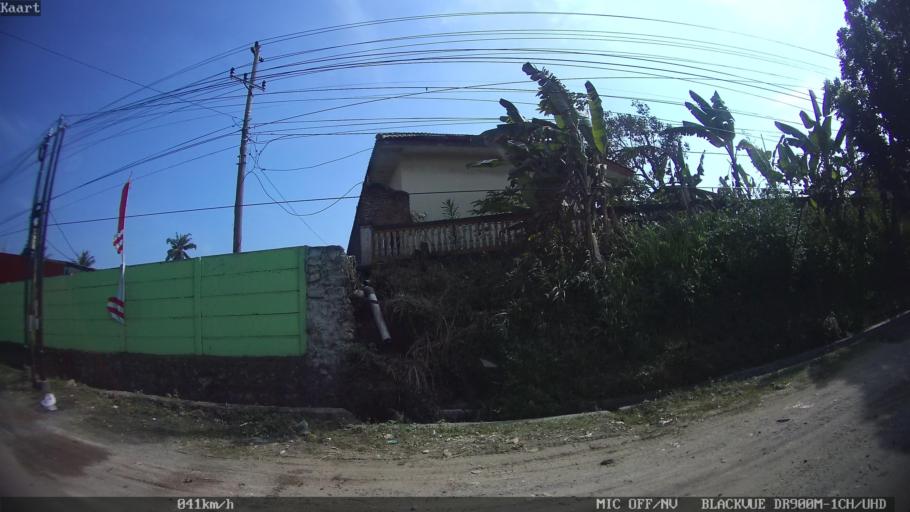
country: ID
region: Lampung
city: Kedaton
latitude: -5.3585
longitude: 105.2526
